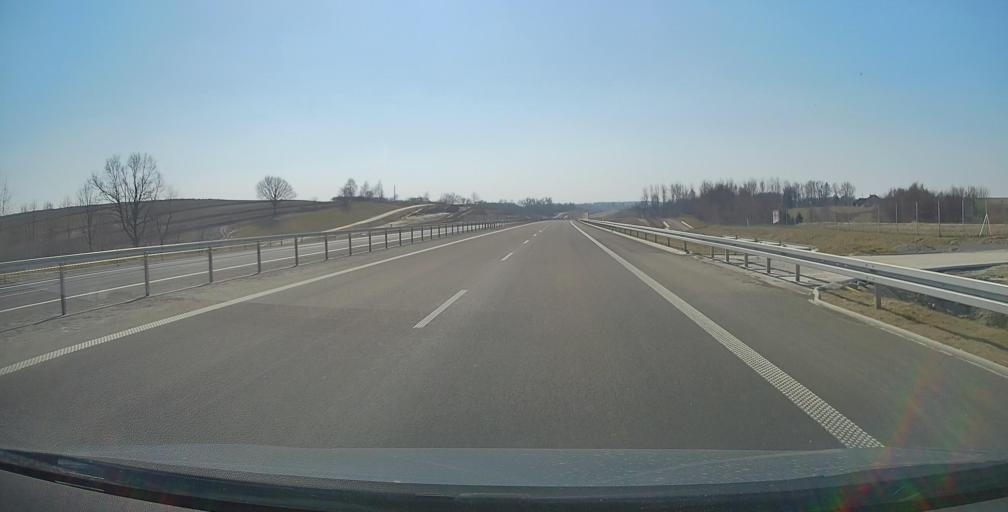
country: PL
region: Lublin Voivodeship
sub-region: Powiat krasnicki
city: Szastarka
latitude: 50.8205
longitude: 22.2993
